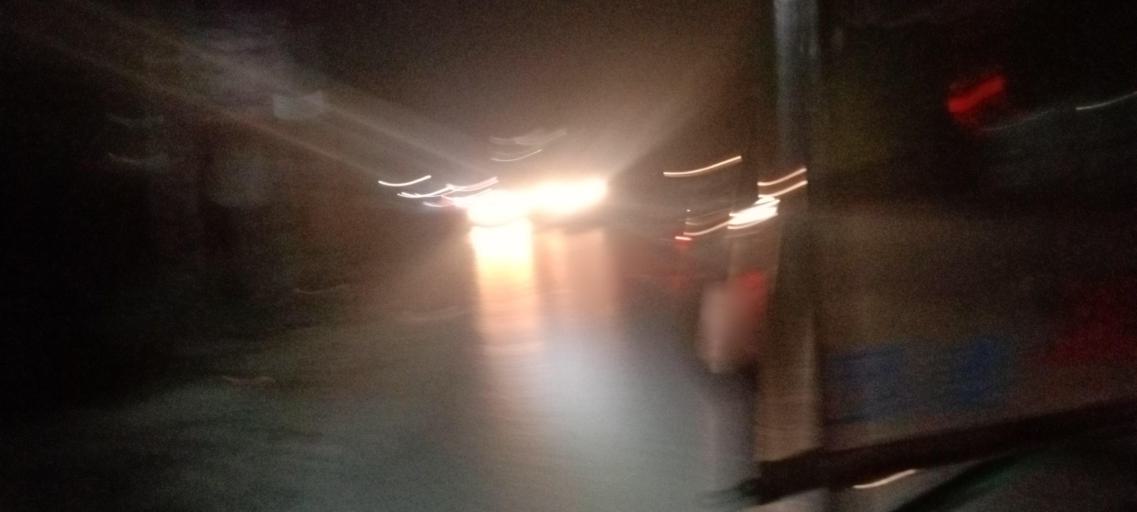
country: BD
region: Dhaka
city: Azimpur
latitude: 23.7000
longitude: 90.3694
